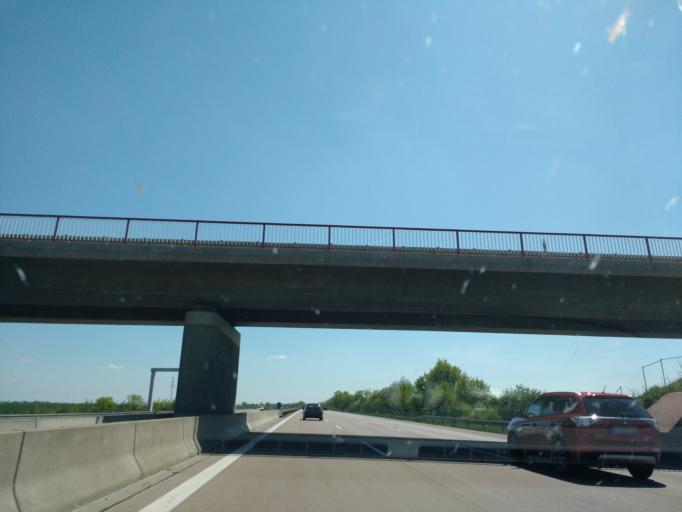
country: DE
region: Saxony-Anhalt
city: Dolbau
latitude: 51.4687
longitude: 12.0890
